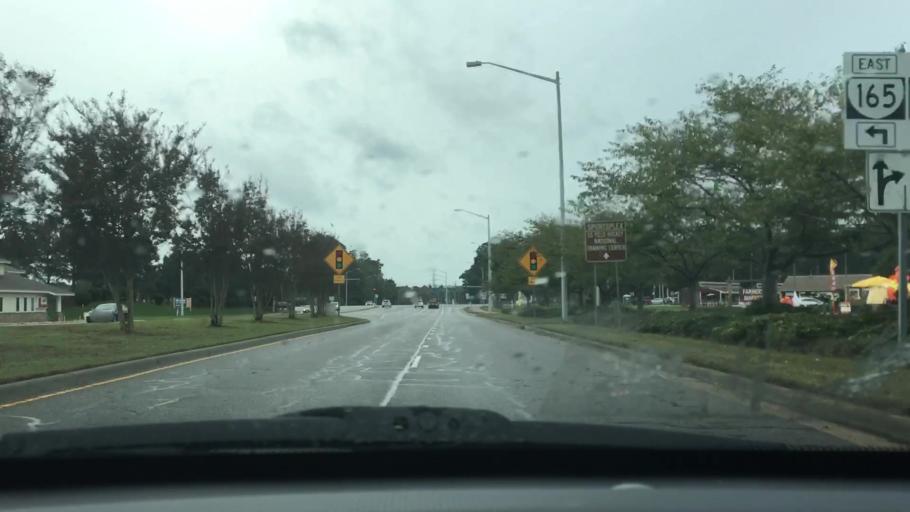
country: US
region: Virginia
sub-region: City of Virginia Beach
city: Virginia Beach
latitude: 36.7768
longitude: -76.0894
